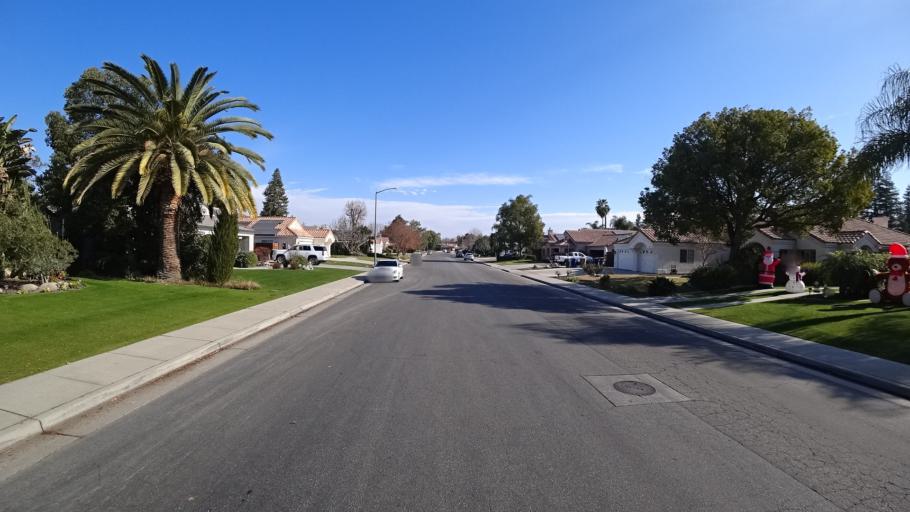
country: US
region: California
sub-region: Kern County
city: Greenacres
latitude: 35.4047
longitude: -119.0868
